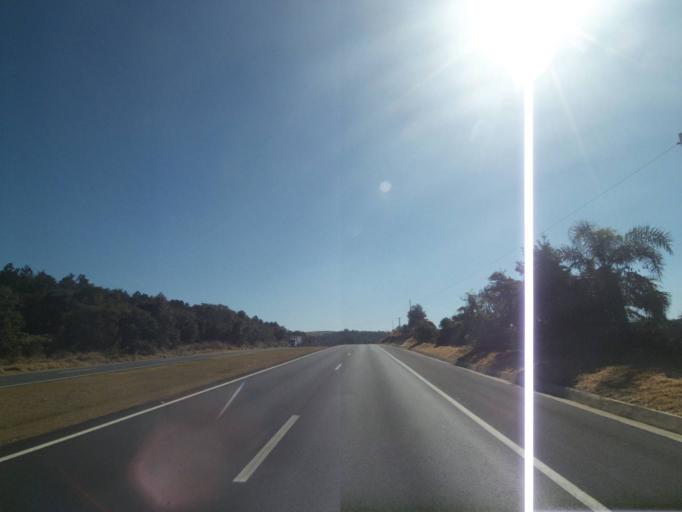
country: BR
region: Parana
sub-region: Carambei
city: Carambei
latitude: -24.8824
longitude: -50.4385
